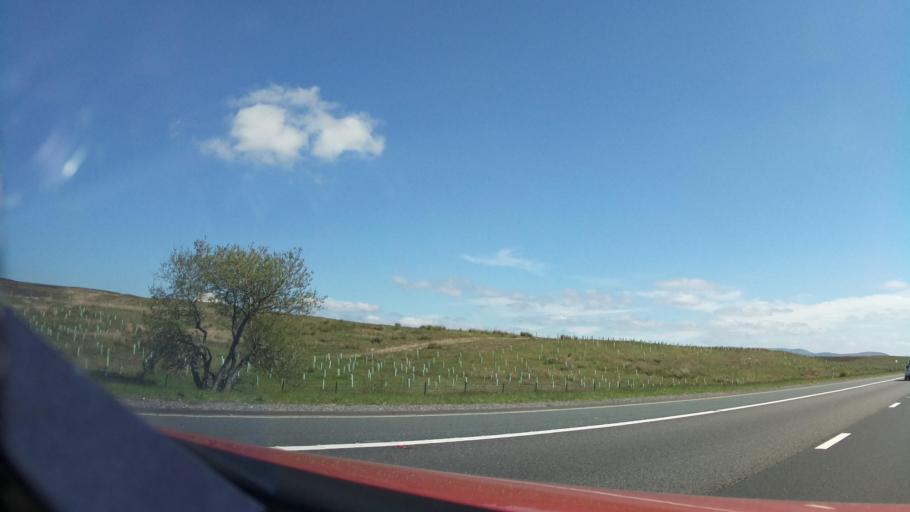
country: GB
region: England
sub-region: Cumbria
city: Appleby-in-Westmorland
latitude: 54.4824
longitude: -2.6329
